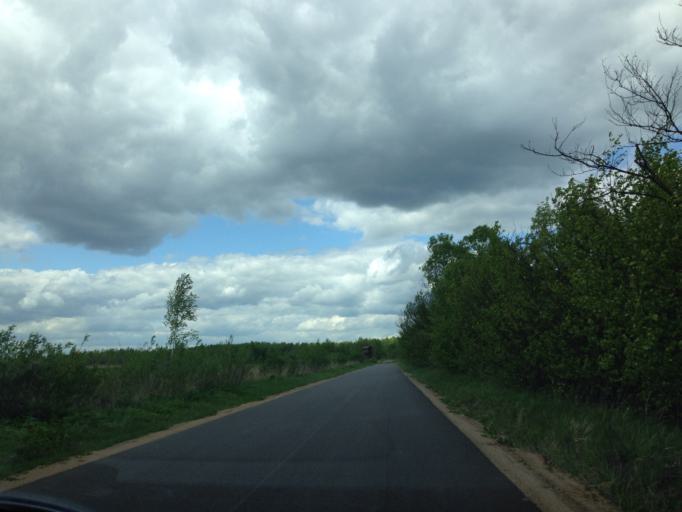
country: PL
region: Podlasie
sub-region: Powiat bialostocki
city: Tykocin
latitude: 53.2963
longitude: 22.6061
